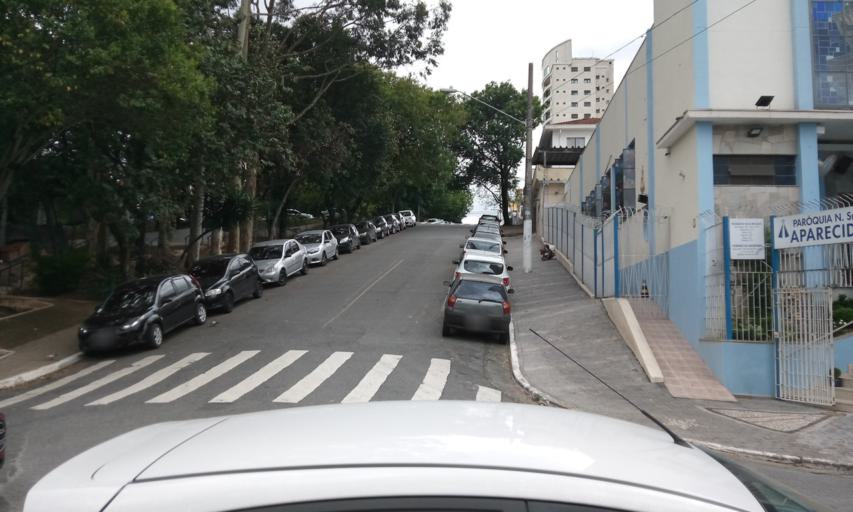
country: BR
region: Sao Paulo
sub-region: Sao Paulo
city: Sao Paulo
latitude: -23.4920
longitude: -46.6158
